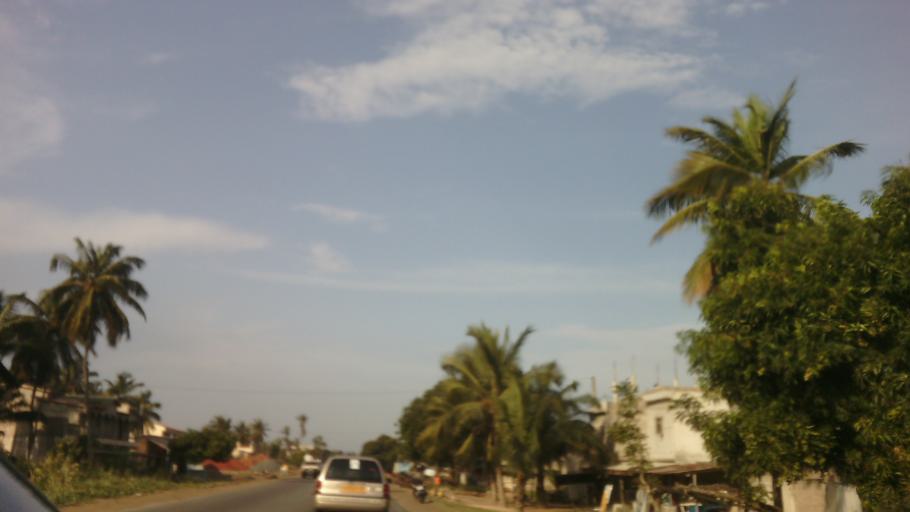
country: TG
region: Maritime
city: Vogan
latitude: 6.1993
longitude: 1.4049
